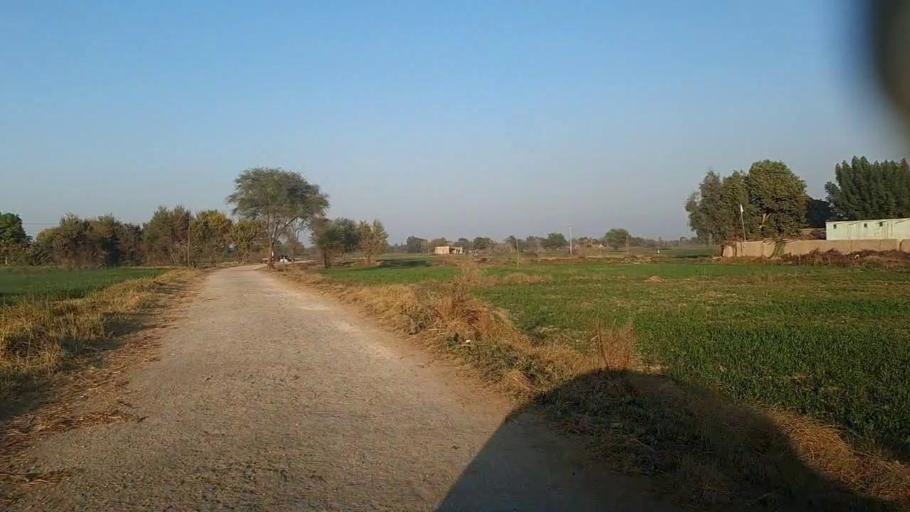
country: PK
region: Sindh
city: Mirpur Mathelo
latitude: 27.8800
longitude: 69.6507
